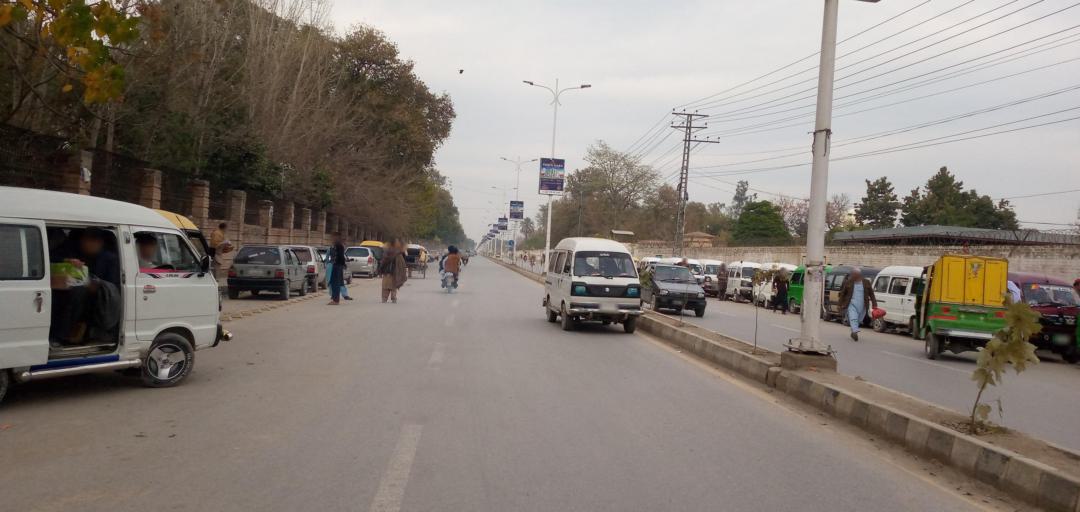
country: PK
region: Khyber Pakhtunkhwa
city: Peshawar
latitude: 33.9988
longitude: 71.4884
